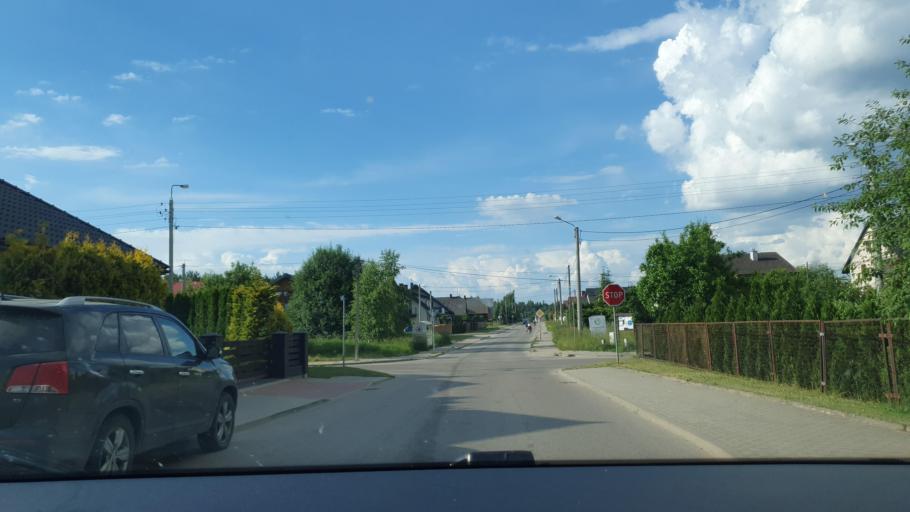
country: PL
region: Podlasie
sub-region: Powiat bialostocki
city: Wasilkow
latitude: 53.1273
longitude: 23.2515
